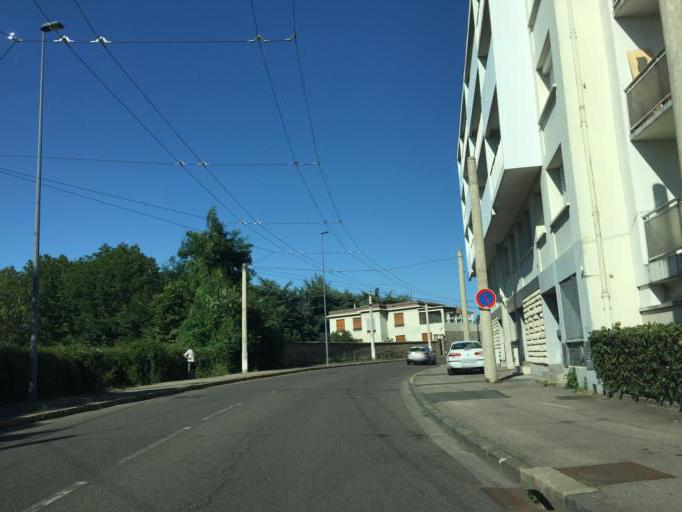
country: FR
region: Rhone-Alpes
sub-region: Departement de la Loire
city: Saint-Etienne
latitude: 45.4408
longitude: 4.4093
